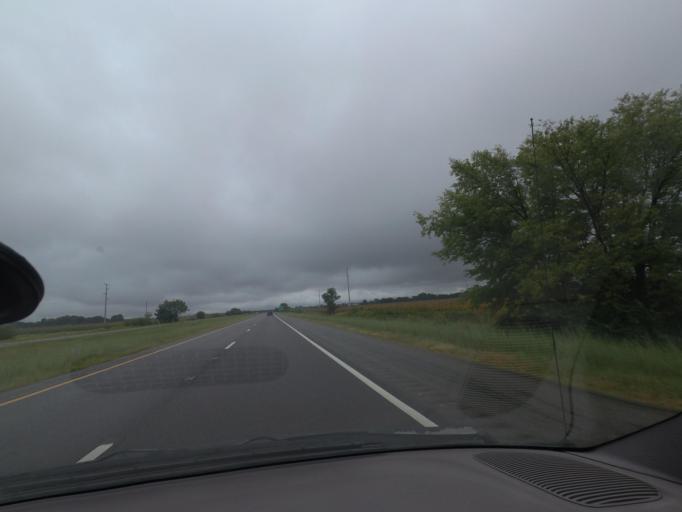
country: US
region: Illinois
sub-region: Champaign County
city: Lake of the Woods
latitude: 40.1204
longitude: -88.3423
